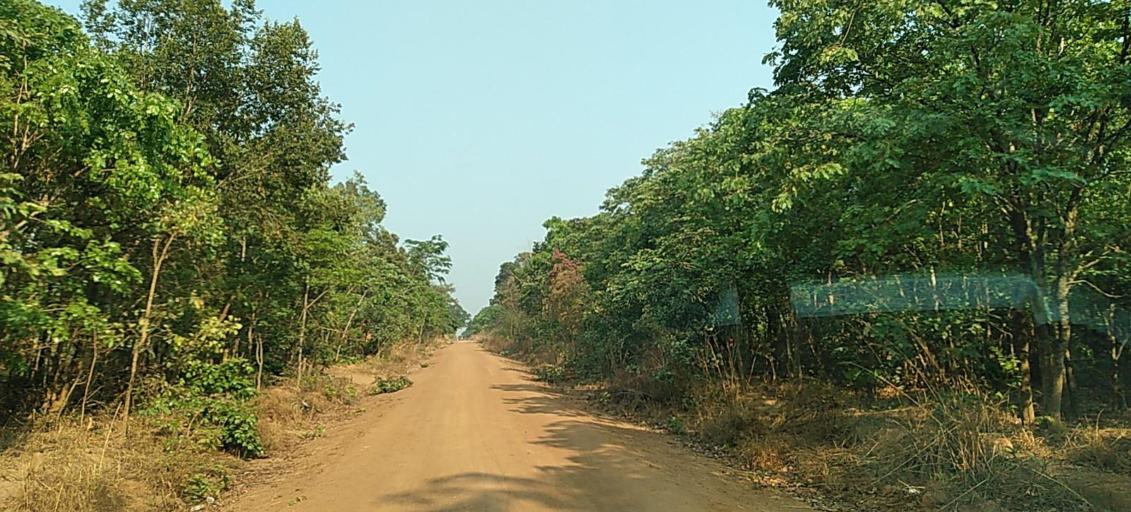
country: ZM
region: Copperbelt
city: Chingola
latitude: -12.8611
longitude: 27.5741
